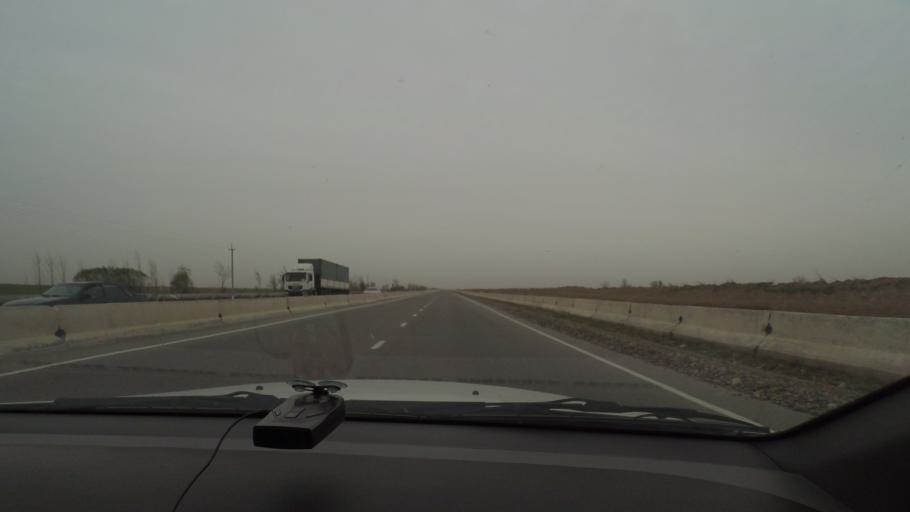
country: UZ
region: Jizzax
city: Dustlik
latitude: 40.4318
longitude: 68.2268
